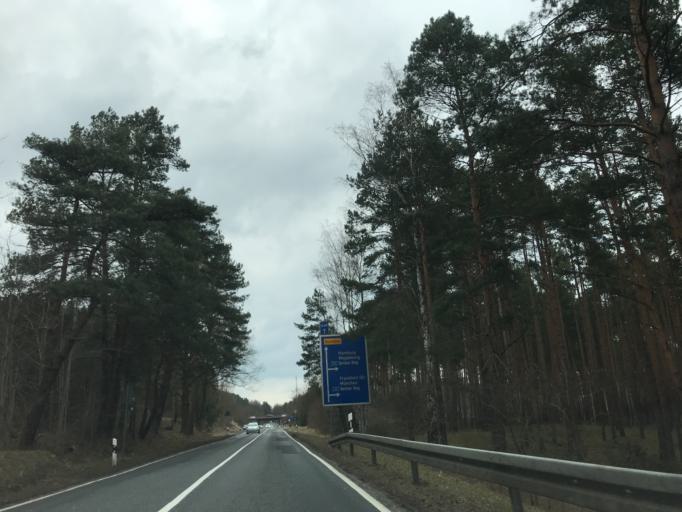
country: DE
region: Brandenburg
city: Fichtenwalde
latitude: 52.3071
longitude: 12.8737
